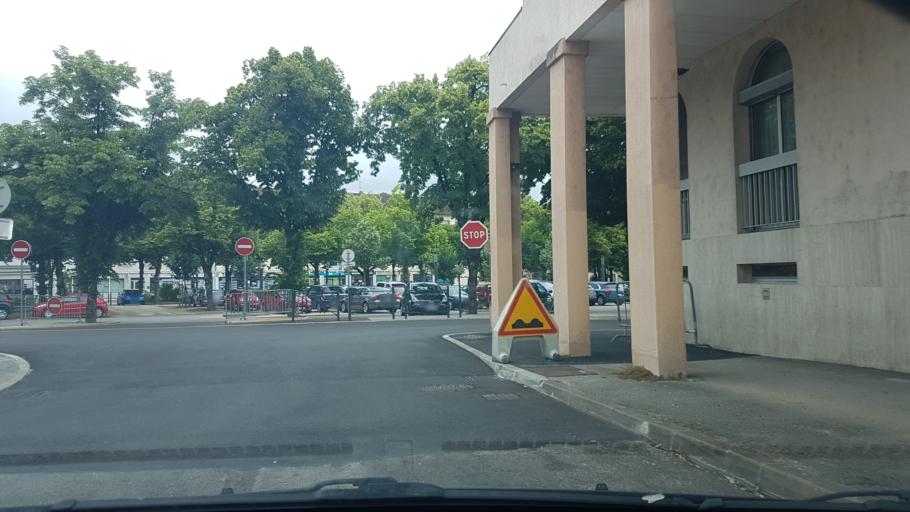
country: FR
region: Franche-Comte
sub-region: Departement du Jura
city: Lons-le-Saunier
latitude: 46.6739
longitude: 5.5588
